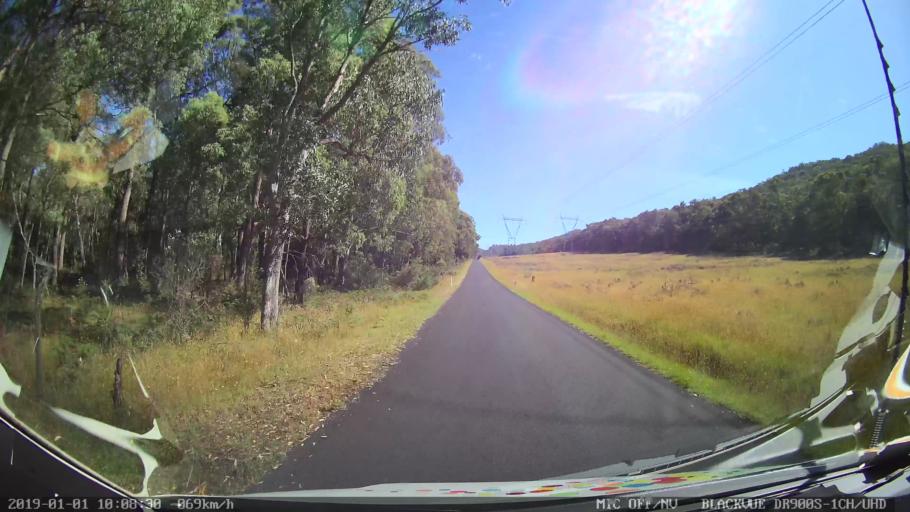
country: AU
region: New South Wales
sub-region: Snowy River
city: Jindabyne
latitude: -36.1587
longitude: 148.1576
